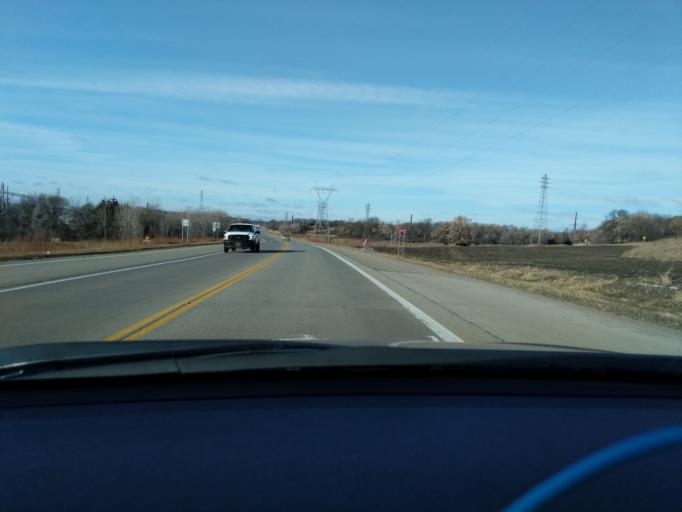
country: US
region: Minnesota
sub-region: Yellow Medicine County
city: Granite Falls
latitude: 44.8045
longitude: -95.5215
